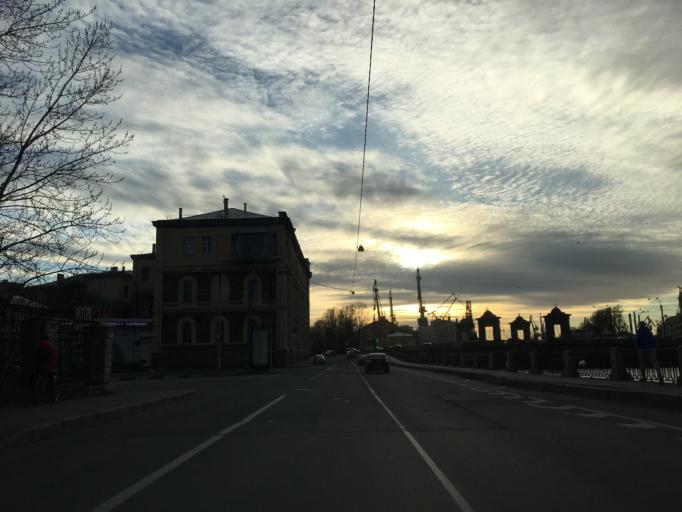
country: RU
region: St.-Petersburg
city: Admiralteisky
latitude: 59.9160
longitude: 30.2821
